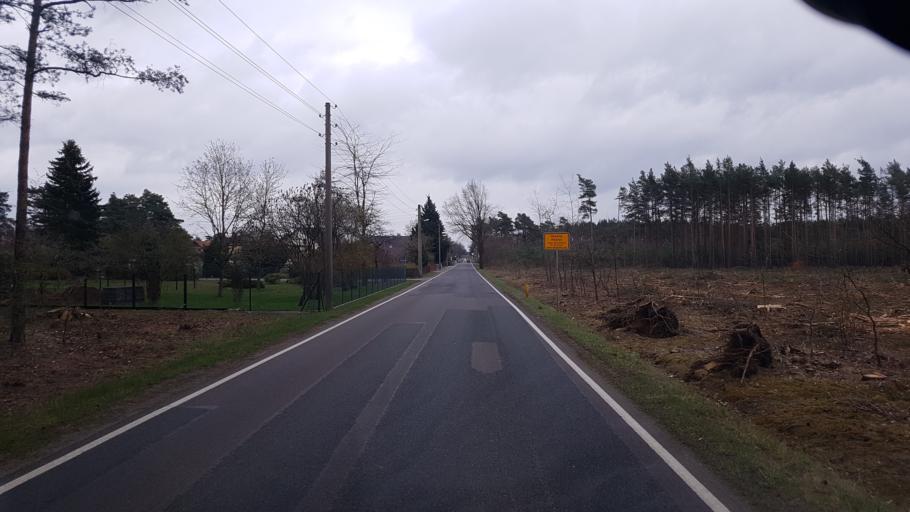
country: DE
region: Brandenburg
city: Hohenbocka
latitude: 51.4529
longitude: 14.0026
